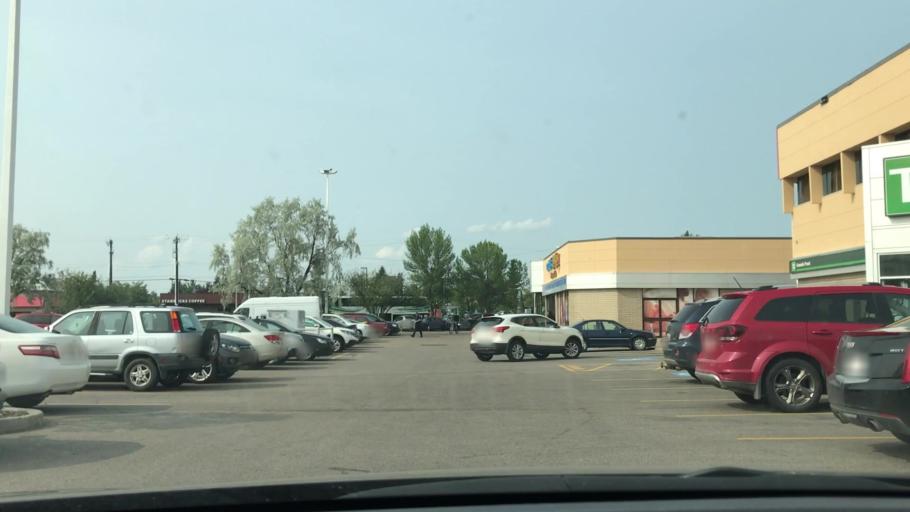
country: CA
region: Alberta
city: Edmonton
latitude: 53.5396
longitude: -113.4237
